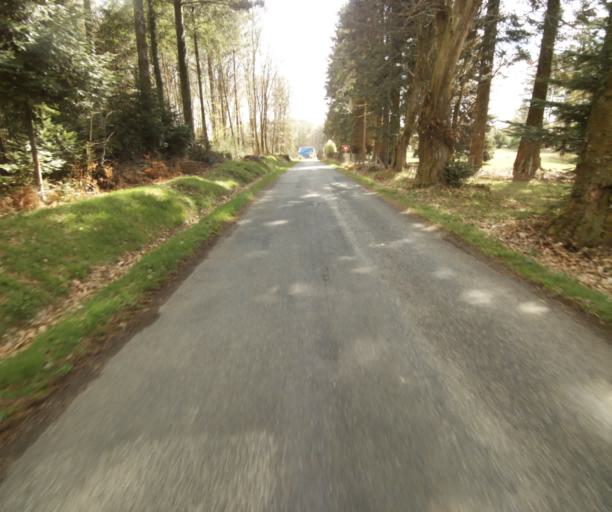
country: FR
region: Limousin
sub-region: Departement de la Correze
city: Correze
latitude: 45.2475
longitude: 1.9415
